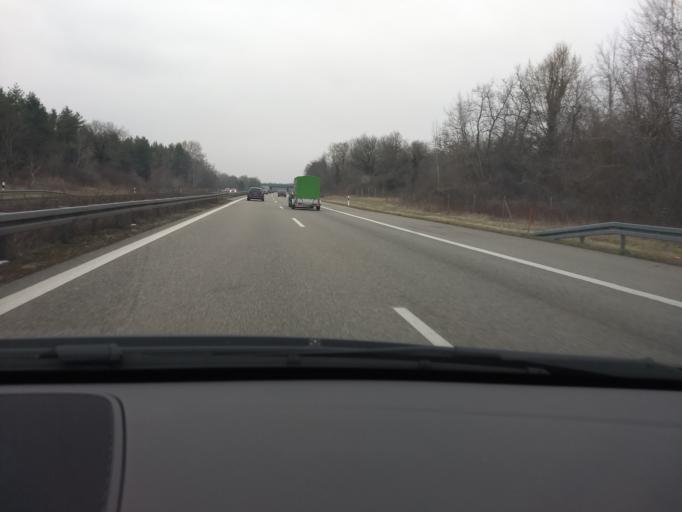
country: FR
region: Alsace
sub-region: Departement du Haut-Rhin
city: Ottmarsheim
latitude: 47.7716
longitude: 7.5366
